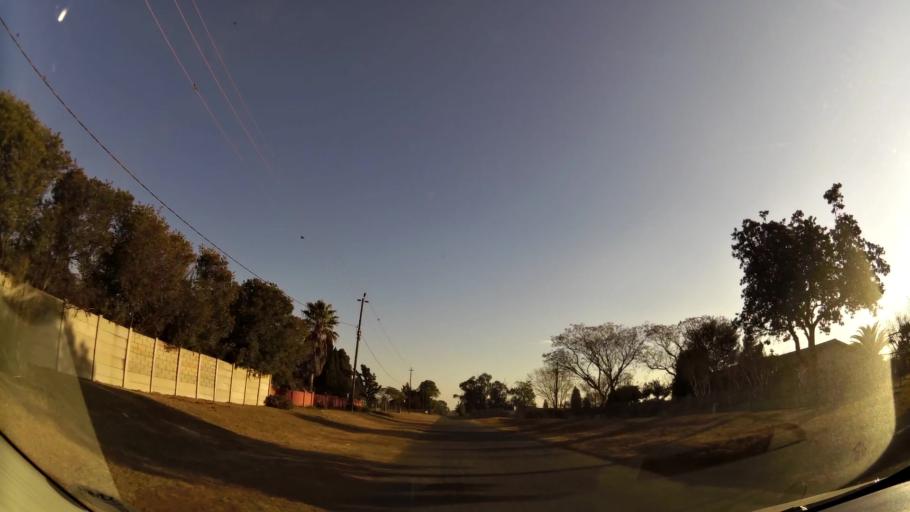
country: ZA
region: Gauteng
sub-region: West Rand District Municipality
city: Randfontein
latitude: -26.2145
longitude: 27.6557
